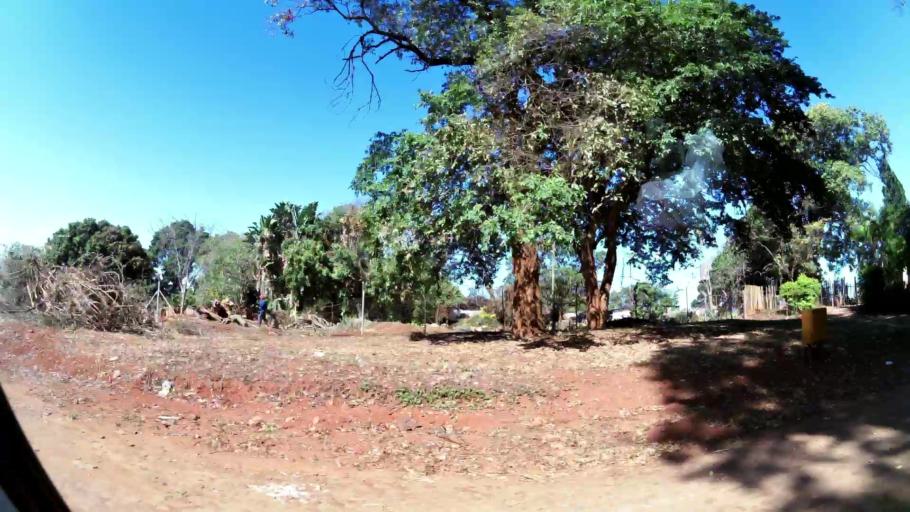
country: ZA
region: Limpopo
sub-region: Mopani District Municipality
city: Tzaneen
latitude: -23.8203
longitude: 30.1567
